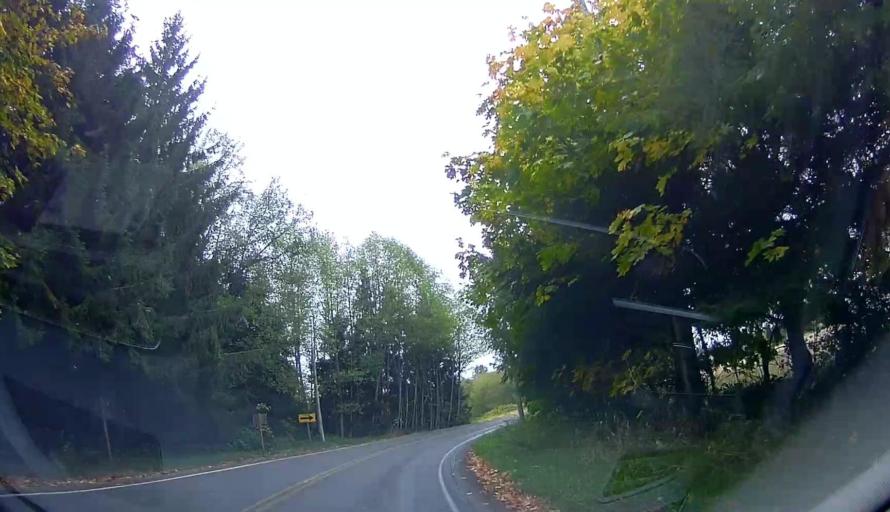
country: US
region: Washington
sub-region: Skagit County
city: Sedro-Woolley
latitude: 48.5034
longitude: -122.1998
